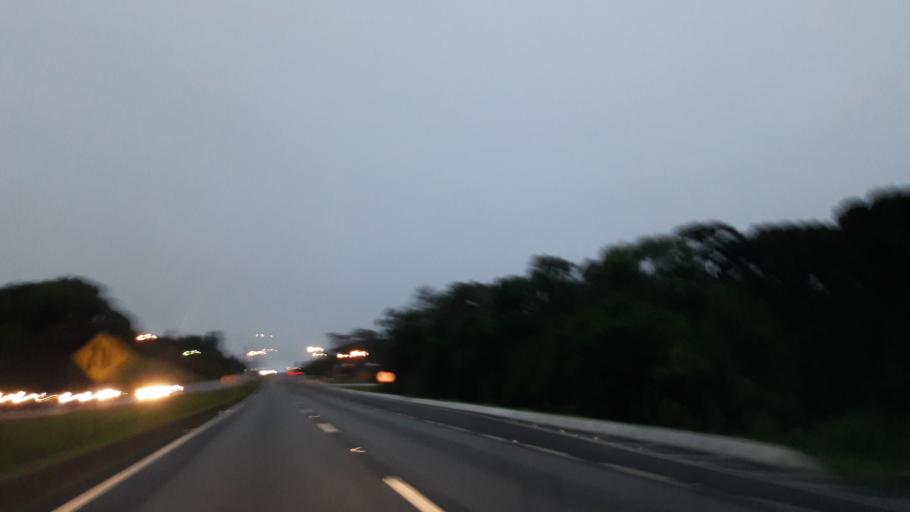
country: BR
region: Parana
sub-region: Piraquara
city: Piraquara
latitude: -25.5546
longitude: -49.0316
